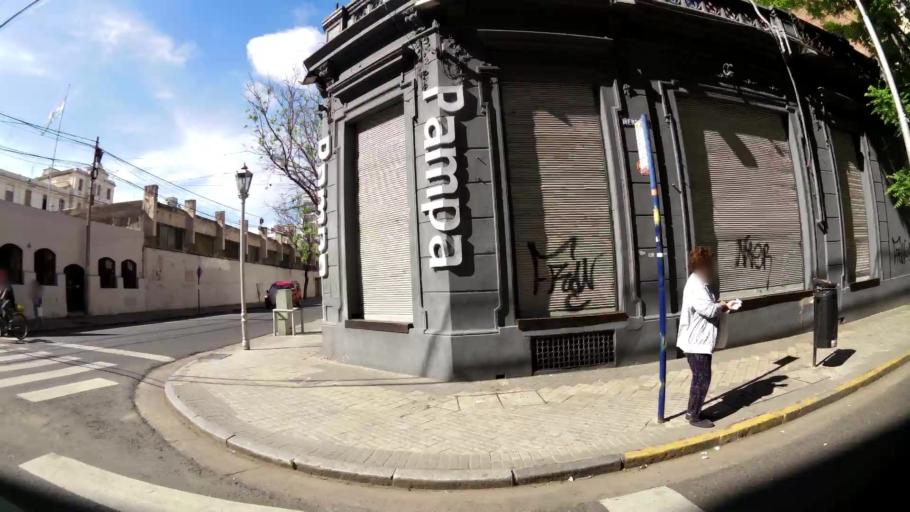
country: AR
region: Santa Fe
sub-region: Departamento de Rosario
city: Rosario
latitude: -32.9493
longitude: -60.6520
